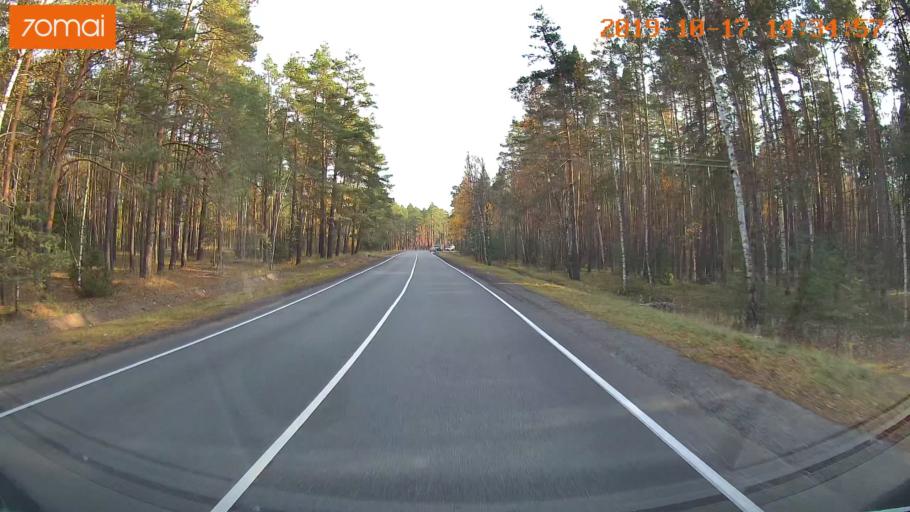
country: RU
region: Rjazan
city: Solotcha
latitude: 54.9057
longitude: 40.0010
